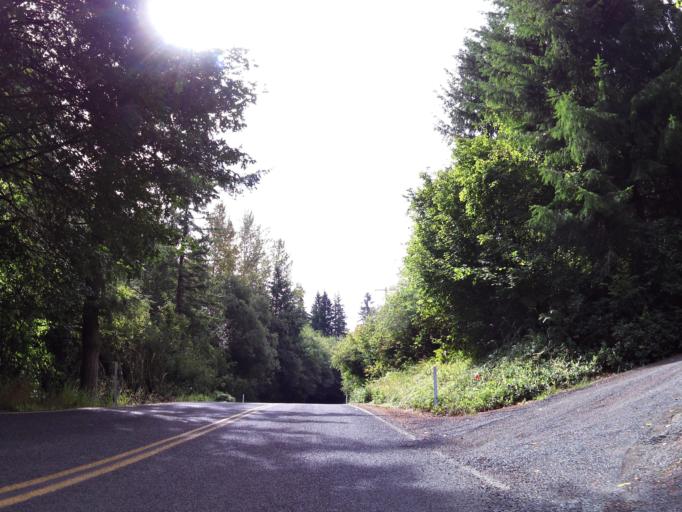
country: US
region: Washington
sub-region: Lewis County
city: Chehalis
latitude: 46.5962
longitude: -122.9711
